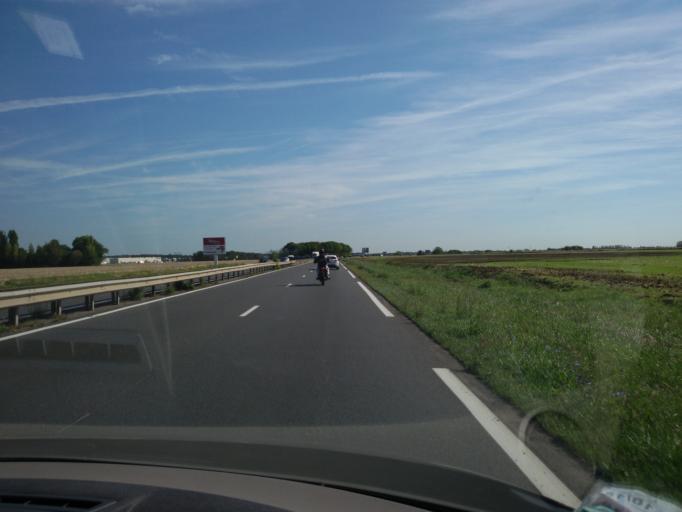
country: FR
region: Ile-de-France
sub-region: Departement de l'Essonne
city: Le Plessis-Pate
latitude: 48.6094
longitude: 2.3341
